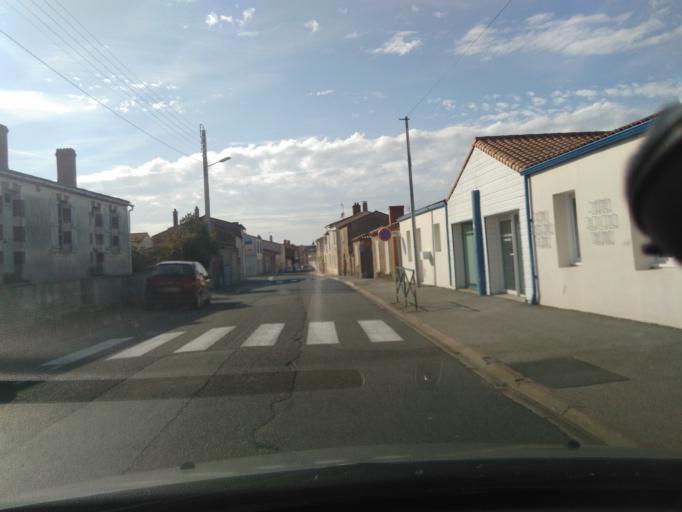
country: FR
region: Pays de la Loire
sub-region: Departement de la Vendee
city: Saint-Hilaire-de-Talmont
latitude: 46.4652
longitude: -1.6129
